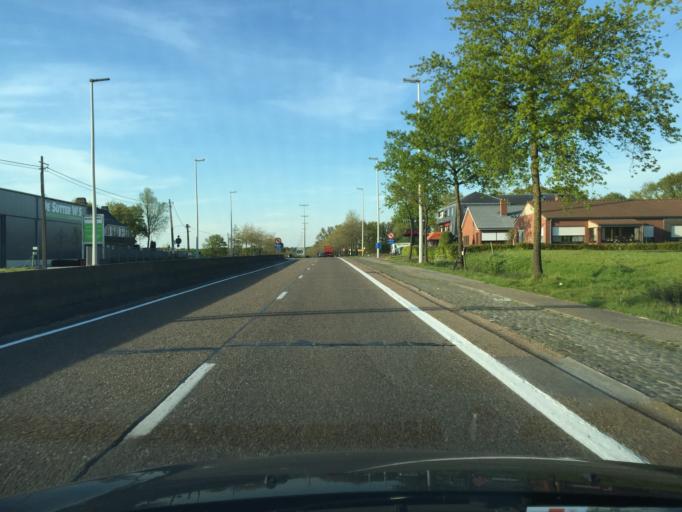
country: BE
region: Flanders
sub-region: Provincie Oost-Vlaanderen
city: Knesselare
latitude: 51.1527
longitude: 3.4324
